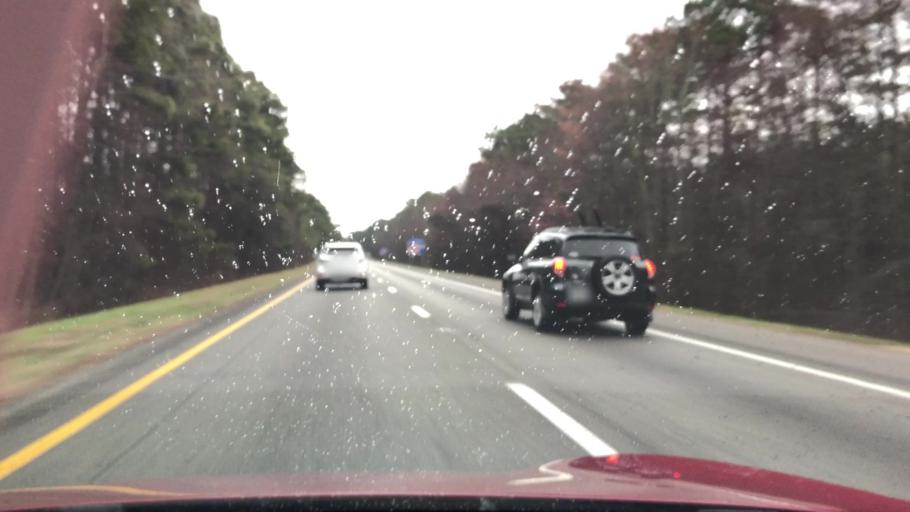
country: US
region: South Carolina
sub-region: Dillon County
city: Latta
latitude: 34.3367
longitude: -79.5485
